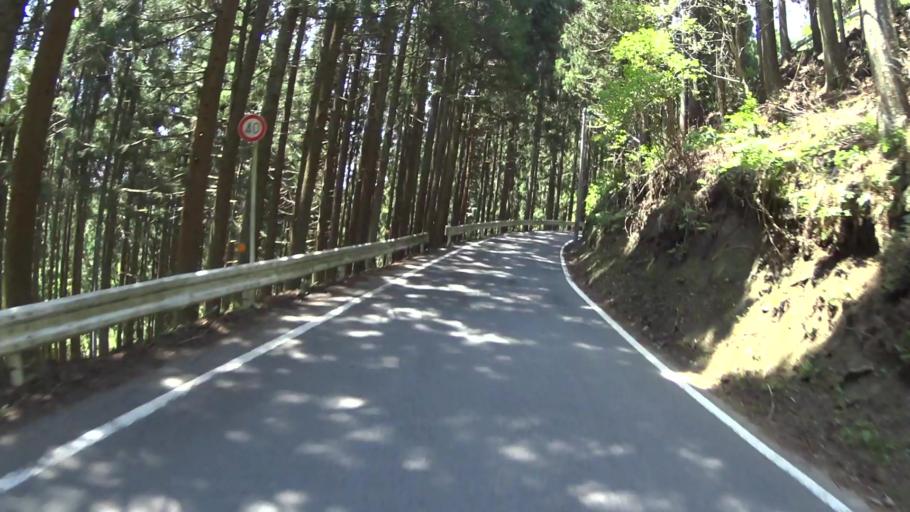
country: JP
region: Shiga Prefecture
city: Kitahama
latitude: 35.1543
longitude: 135.7894
